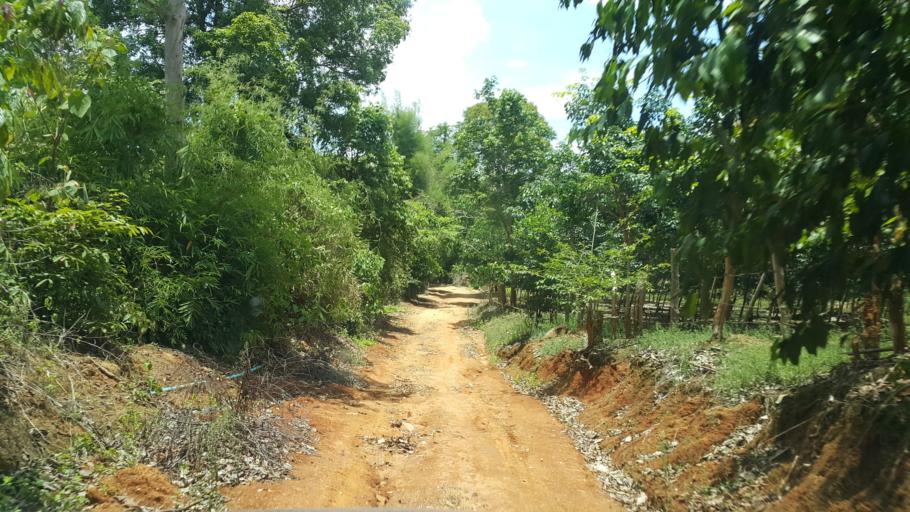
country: TH
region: Phayao
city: Phayao
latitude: 19.1800
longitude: 99.7717
